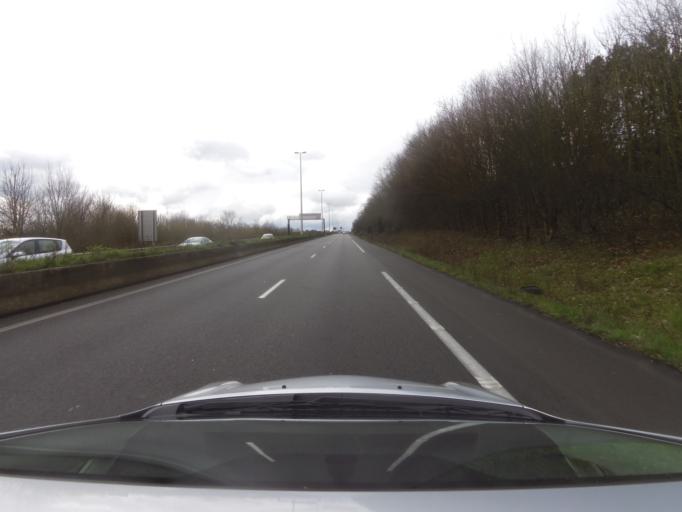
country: FR
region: Nord-Pas-de-Calais
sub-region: Departement du Pas-de-Calais
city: Wimille
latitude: 50.7568
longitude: 1.6314
